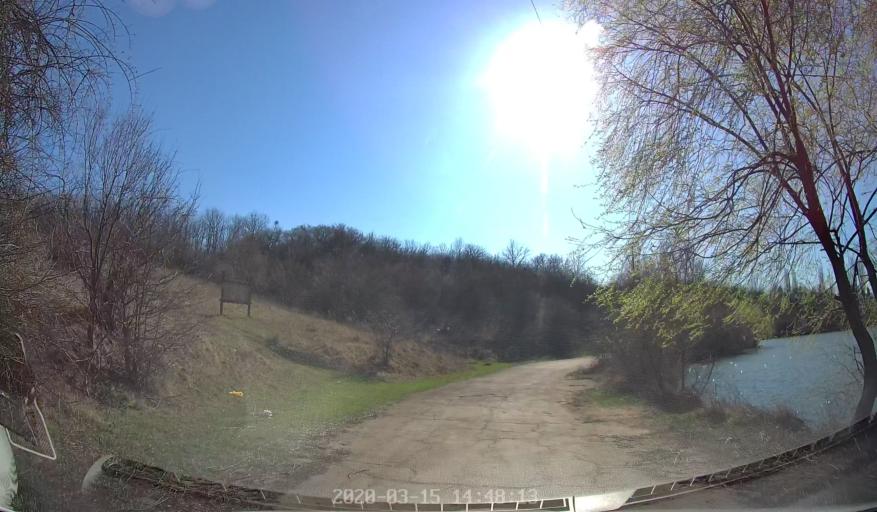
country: MD
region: Orhei
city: Orhei
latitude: 47.2806
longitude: 28.8315
